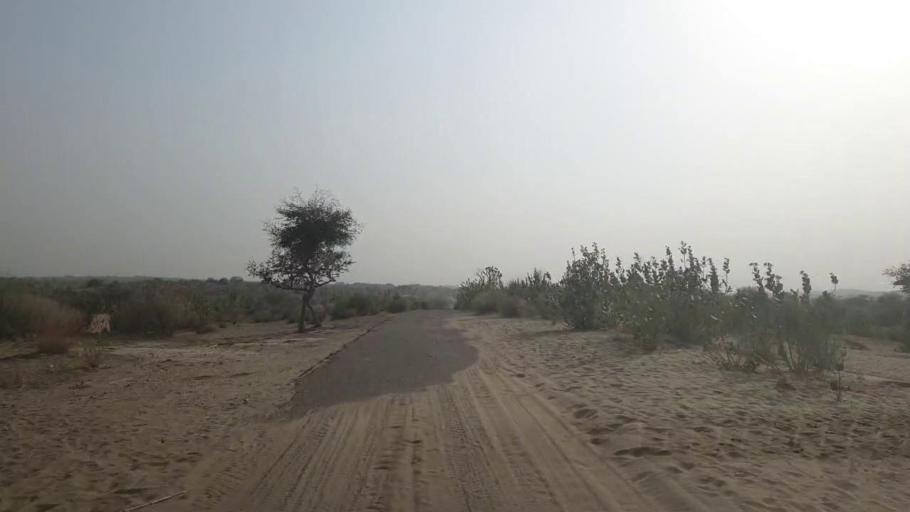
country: PK
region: Sindh
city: Chor
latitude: 25.4749
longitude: 69.9721
